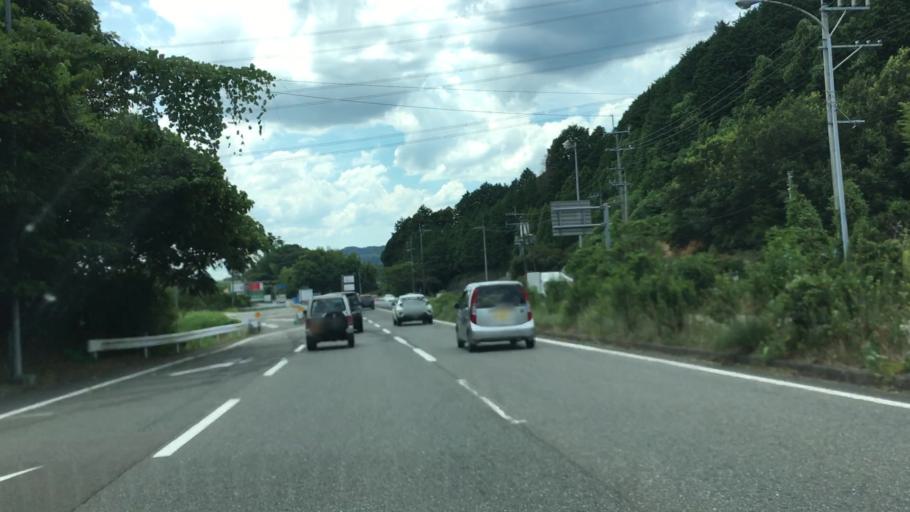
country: JP
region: Fukuoka
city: Chikushino-shi
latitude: 33.4413
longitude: 130.5274
